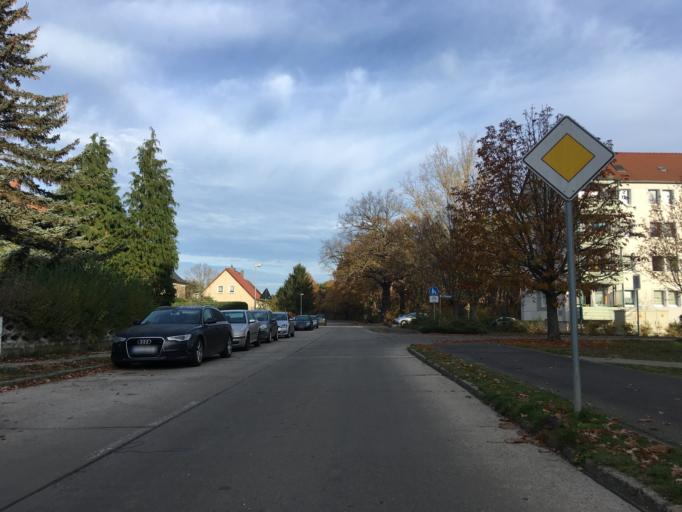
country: DE
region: Brandenburg
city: Luebben
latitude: 51.9497
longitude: 13.8848
